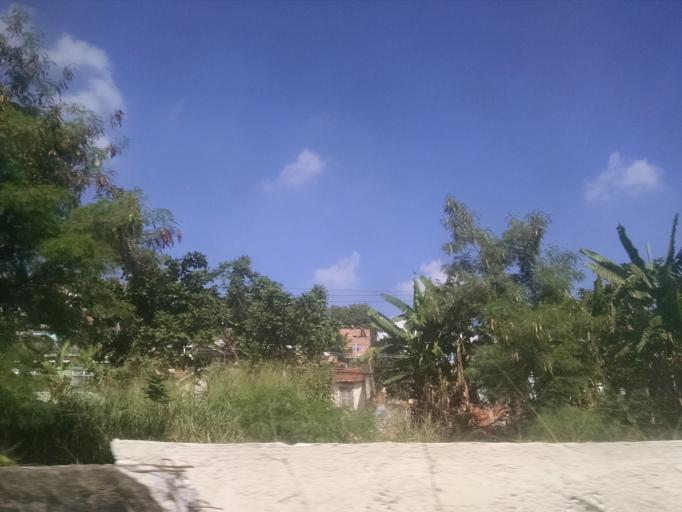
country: BR
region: Rio de Janeiro
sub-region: Duque De Caxias
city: Duque de Caxias
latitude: -22.8701
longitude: -43.2904
